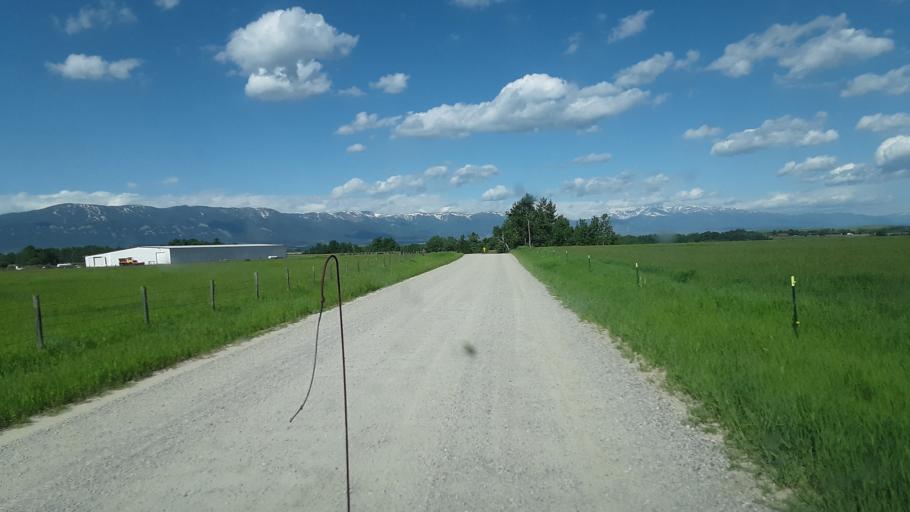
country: US
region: Montana
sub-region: Carbon County
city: Red Lodge
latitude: 45.2786
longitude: -109.1979
